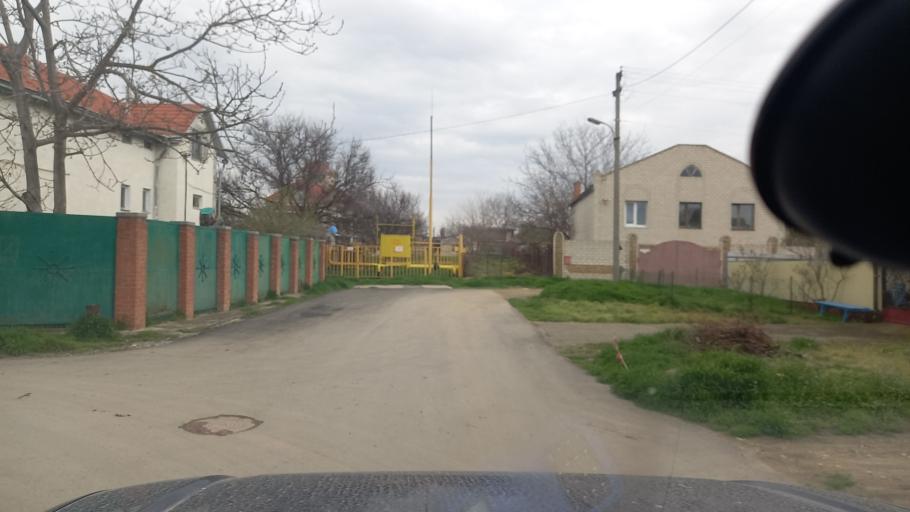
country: RU
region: Krasnodarskiy
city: Tsibanobalka
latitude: 44.9664
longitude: 37.3201
